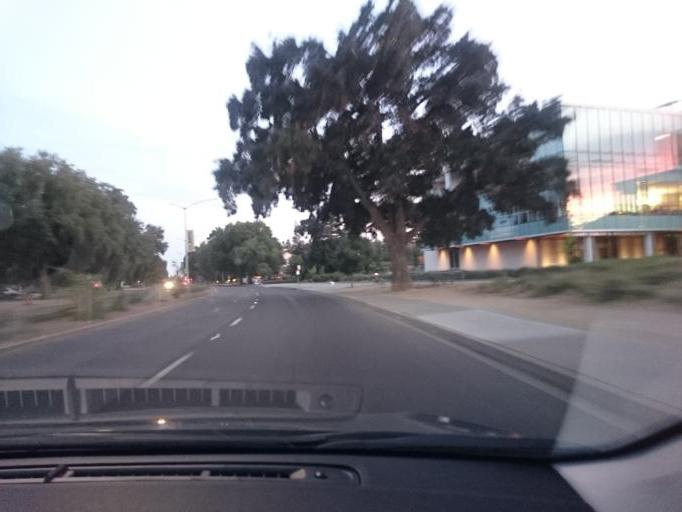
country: US
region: California
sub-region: Yolo County
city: Davis
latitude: 38.5431
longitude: -121.7607
